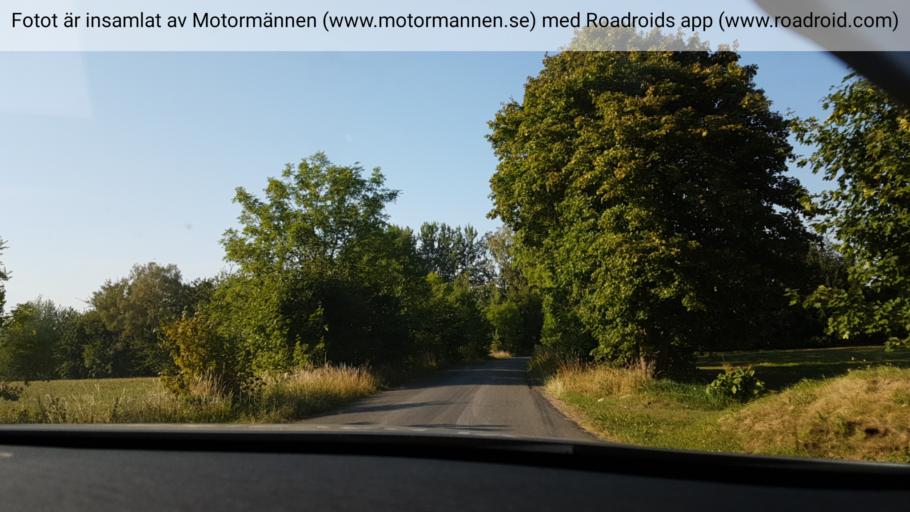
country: SE
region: Vaestra Goetaland
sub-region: Skovde Kommun
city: Stopen
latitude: 58.5124
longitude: 13.7822
